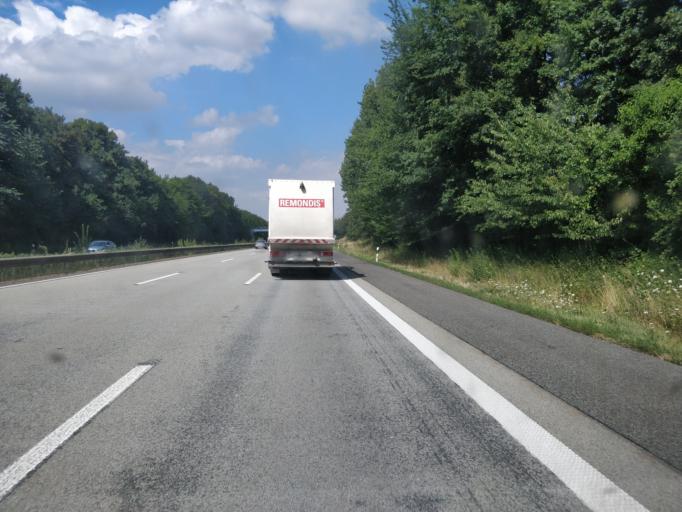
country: DE
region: Rheinland-Pfalz
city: Dernau
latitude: 50.5773
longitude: 7.0737
